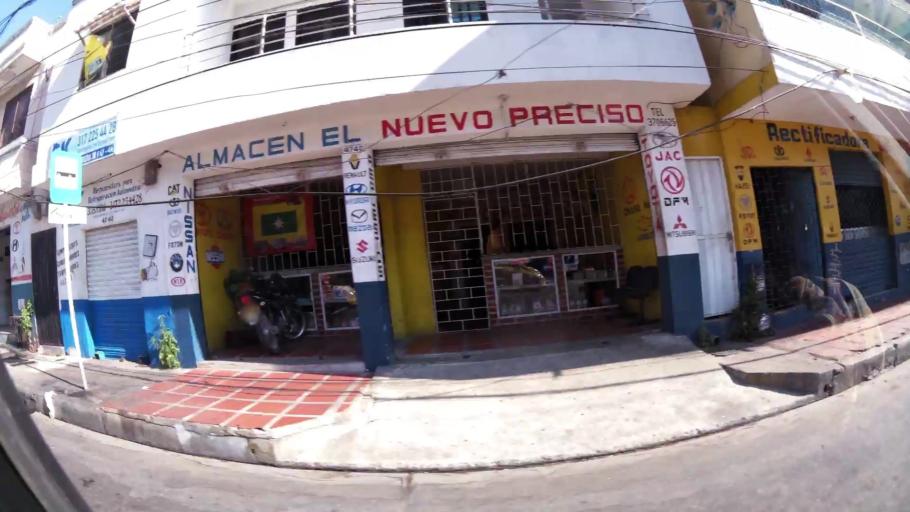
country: CO
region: Atlantico
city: Barranquilla
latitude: 10.9802
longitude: -74.7886
